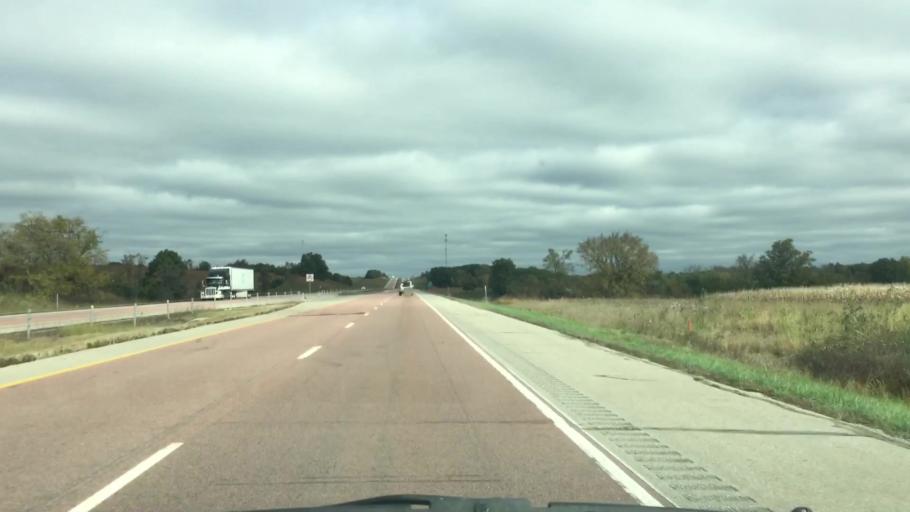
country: US
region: Iowa
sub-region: Clarke County
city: Osceola
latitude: 41.2049
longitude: -93.7860
